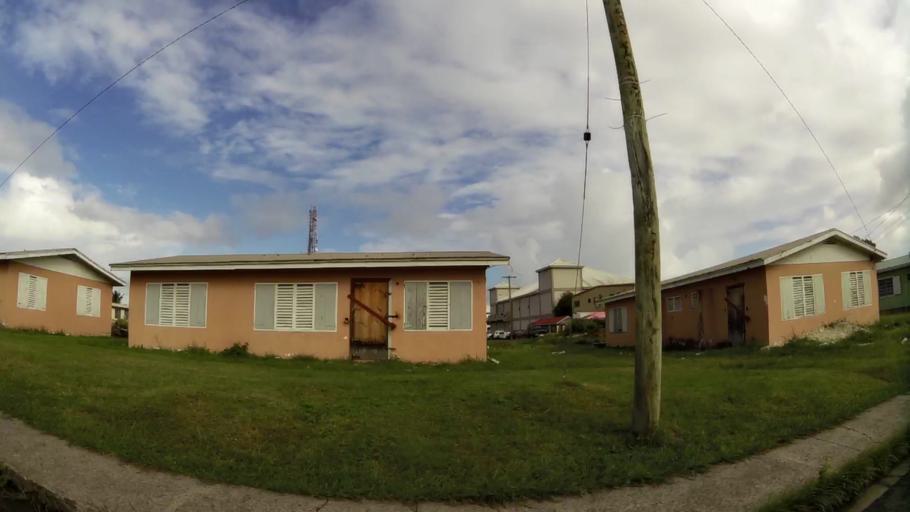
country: AG
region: Saint John
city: Saint John's
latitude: 17.1260
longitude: -61.8228
